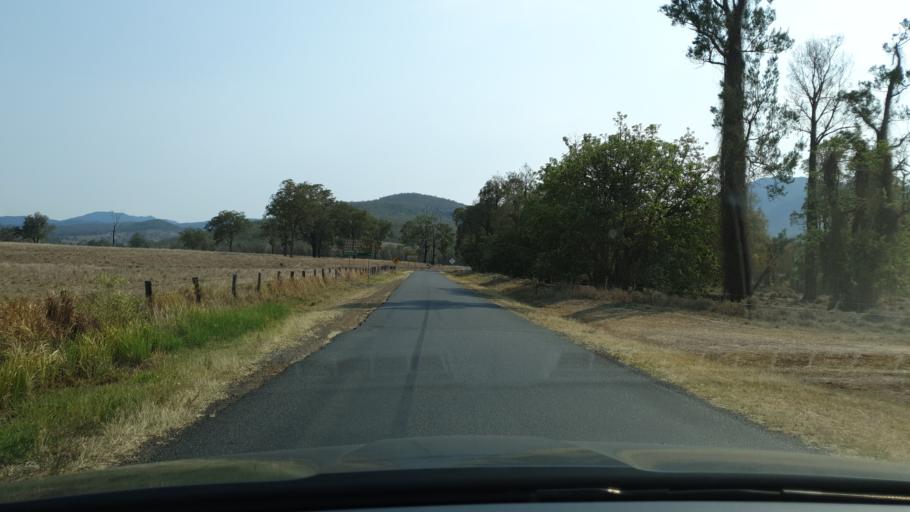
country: AU
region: Queensland
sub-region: Southern Downs
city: Warwick
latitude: -28.1828
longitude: 152.5463
